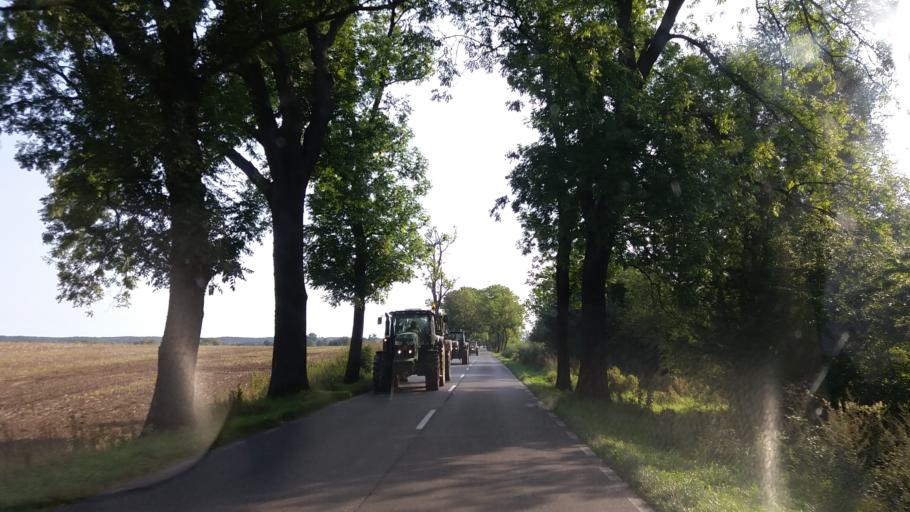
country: PL
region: West Pomeranian Voivodeship
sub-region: Powiat choszczenski
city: Choszczno
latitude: 53.1746
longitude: 15.4832
